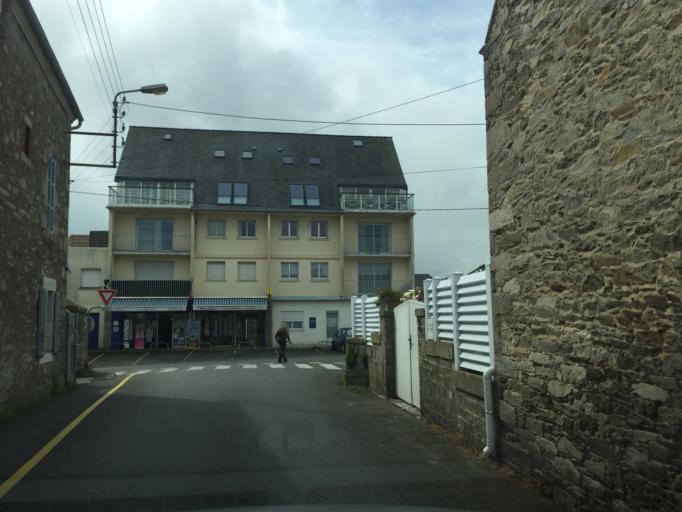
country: FR
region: Brittany
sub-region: Departement des Cotes-d'Armor
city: Saint-Cast-le-Guildo
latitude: 48.6378
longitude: -2.2582
